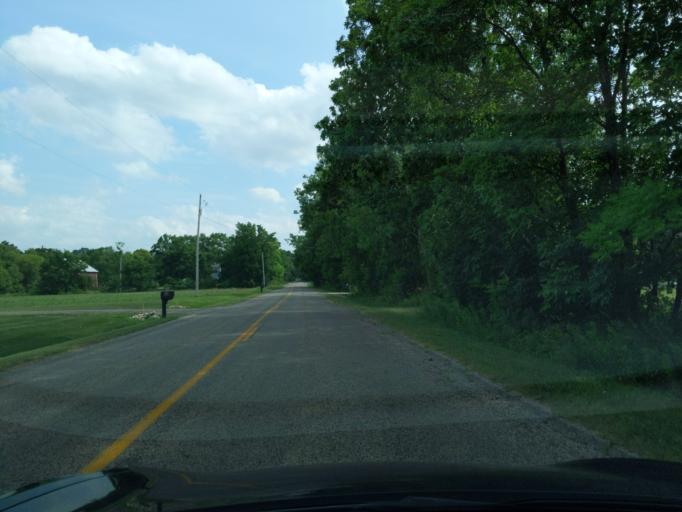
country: US
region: Michigan
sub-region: Eaton County
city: Eaton Rapids
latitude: 42.5270
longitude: -84.6016
